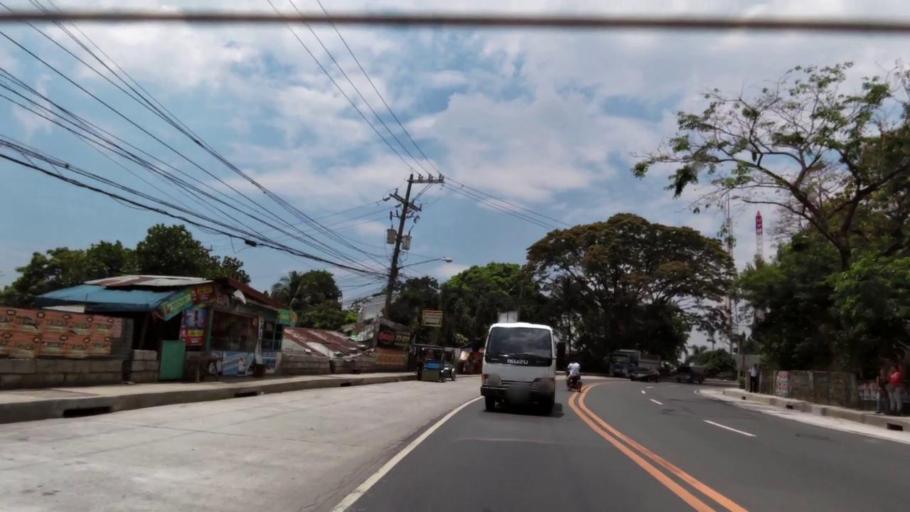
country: PH
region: Calabarzon
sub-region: Province of Rizal
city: Antipolo
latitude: 14.6072
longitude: 121.1661
